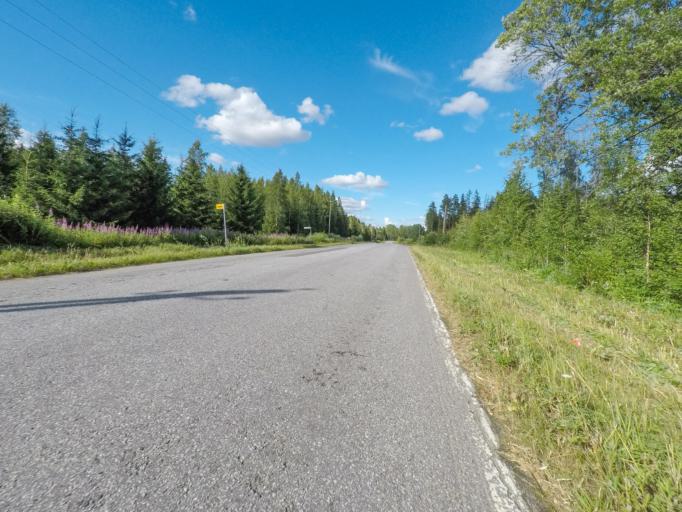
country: FI
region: South Karelia
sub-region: Imatra
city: Imatra
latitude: 61.1381
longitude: 28.7378
